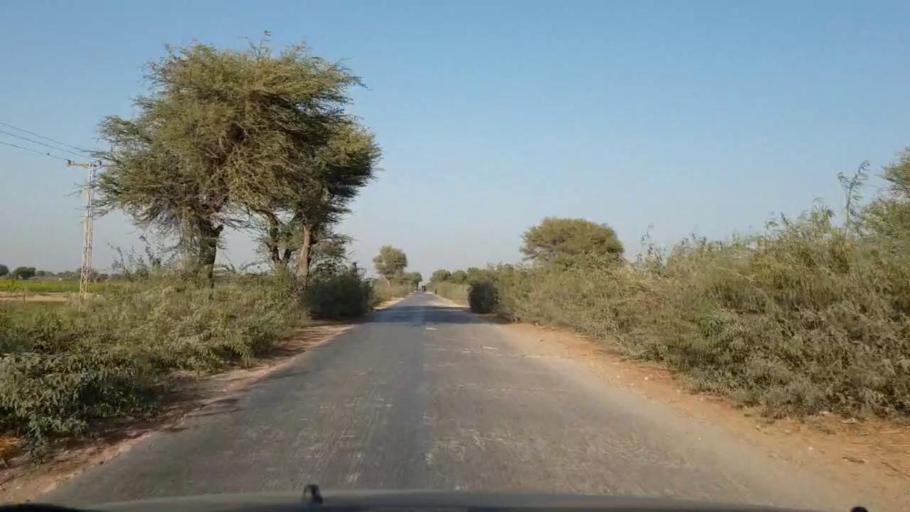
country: PK
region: Sindh
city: Chambar
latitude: 25.2675
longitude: 68.8013
